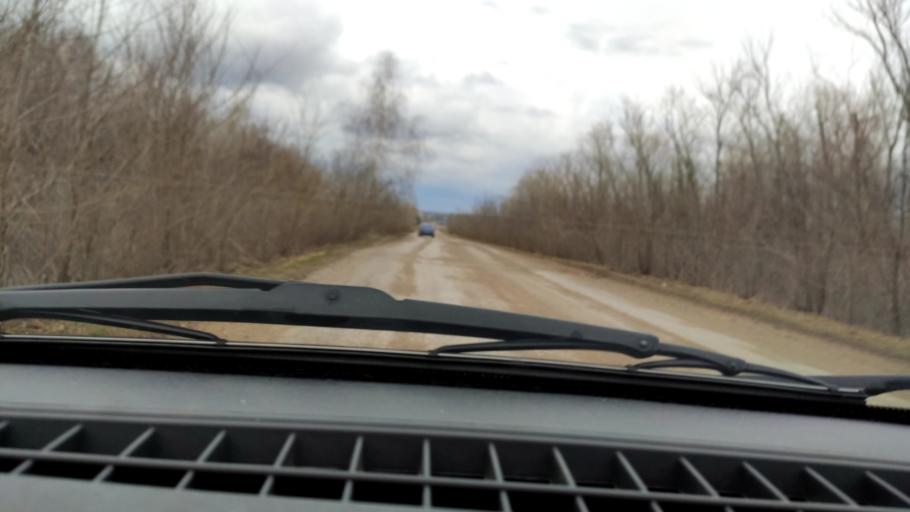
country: RU
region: Bashkortostan
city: Semiletka
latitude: 55.2749
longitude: 54.6451
